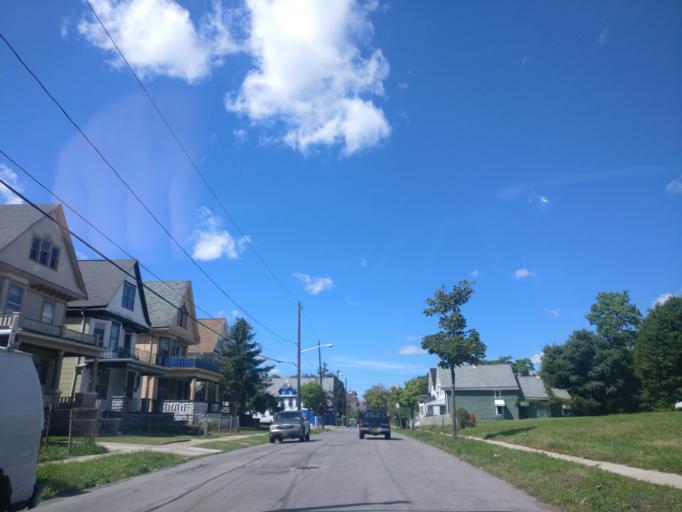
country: US
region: New York
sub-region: Erie County
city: Buffalo
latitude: 42.9094
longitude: -78.8580
